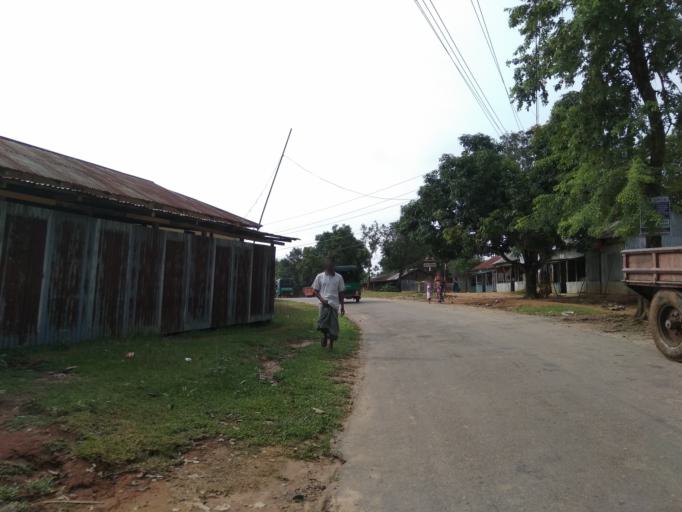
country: BD
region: Chittagong
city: Khagrachhari
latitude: 23.0005
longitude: 92.0093
